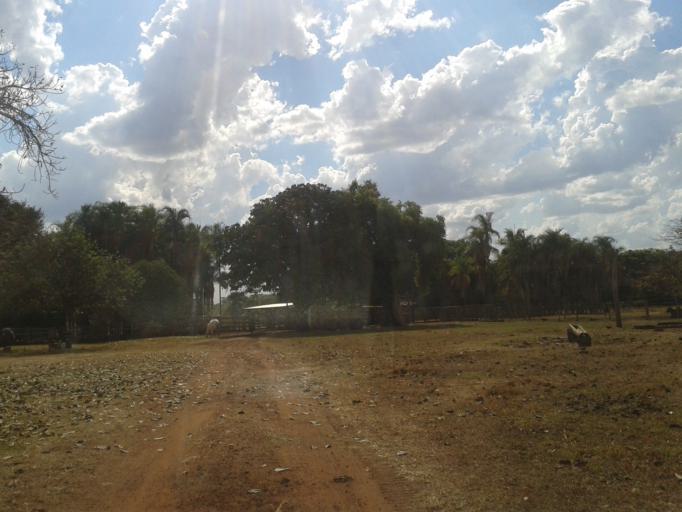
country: BR
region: Minas Gerais
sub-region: Santa Vitoria
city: Santa Vitoria
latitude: -19.1866
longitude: -49.9786
